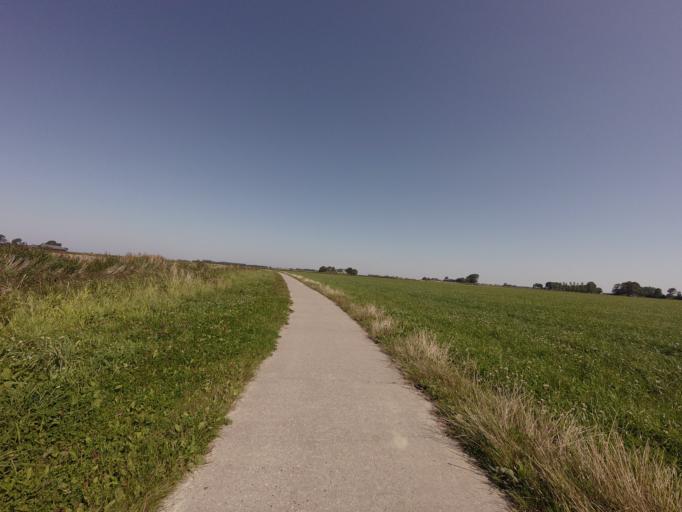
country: NL
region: Friesland
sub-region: Gemeente Dongeradeel
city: Anjum
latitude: 53.3860
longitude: 6.0645
